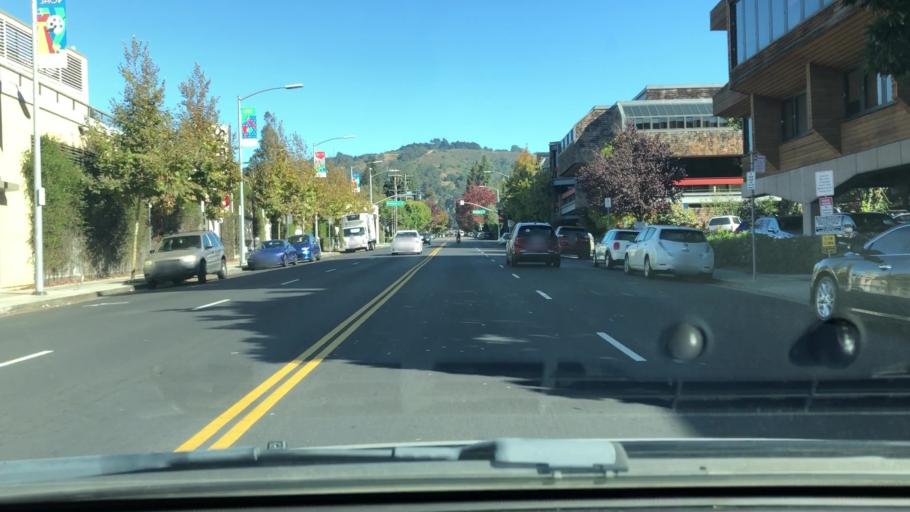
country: US
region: California
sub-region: Alameda County
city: Berkeley
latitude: 37.8500
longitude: -122.2518
